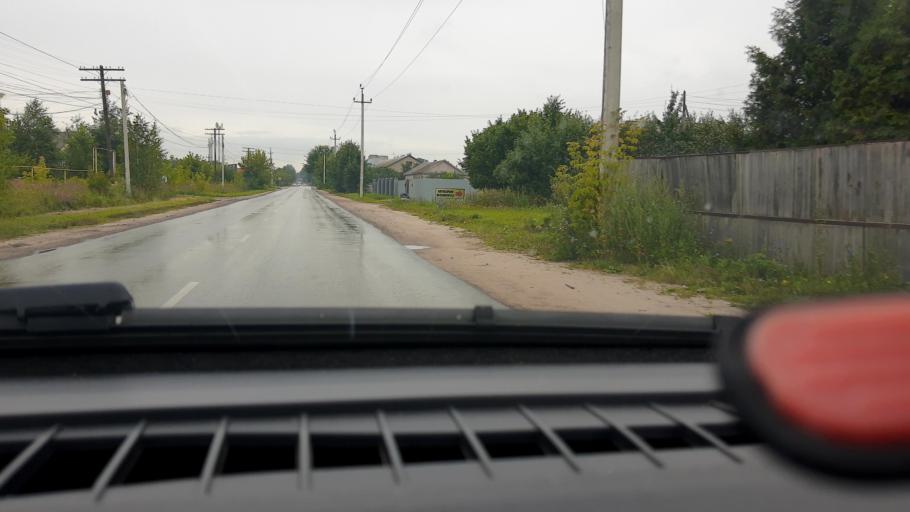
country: RU
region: Nizjnij Novgorod
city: Bor
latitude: 56.3536
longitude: 44.1085
